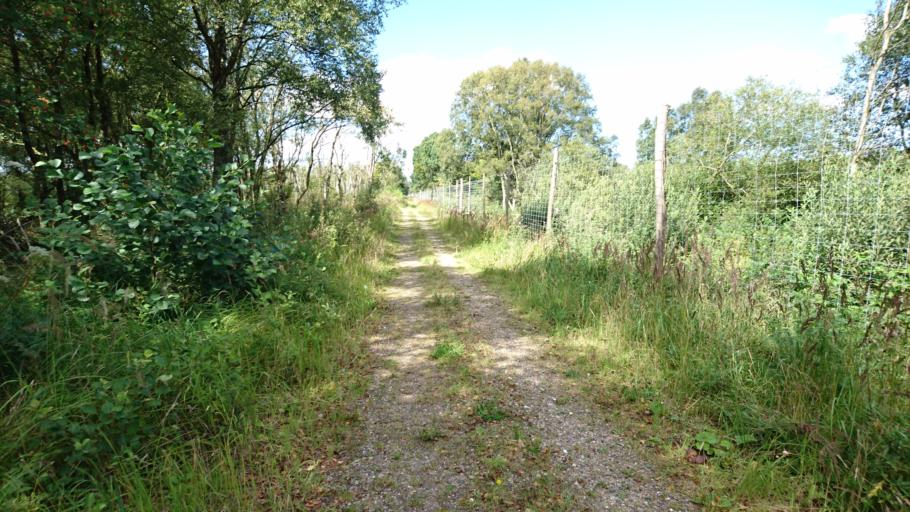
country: DK
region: North Denmark
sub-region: Alborg Kommune
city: Storvorde
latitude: 56.9346
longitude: 10.1865
